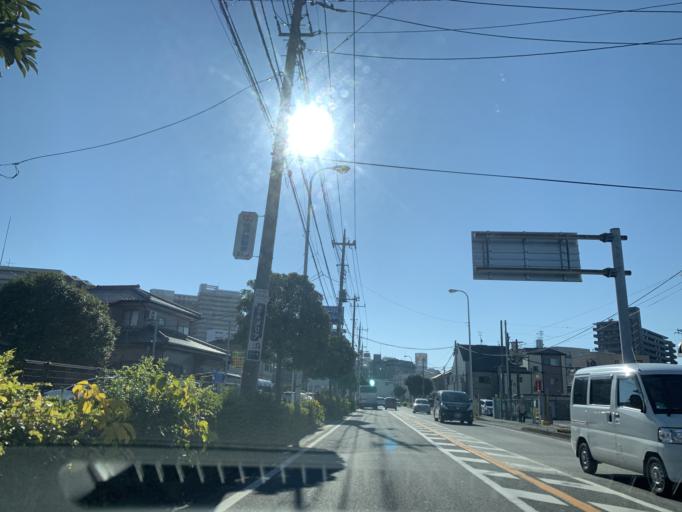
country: JP
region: Chiba
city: Matsudo
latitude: 35.7903
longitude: 139.8990
